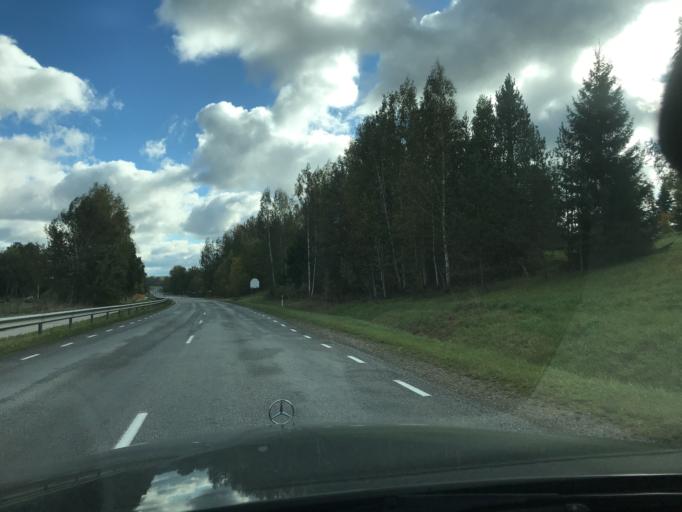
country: EE
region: Vorumaa
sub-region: Antsla vald
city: Vana-Antsla
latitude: 57.9283
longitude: 26.3252
